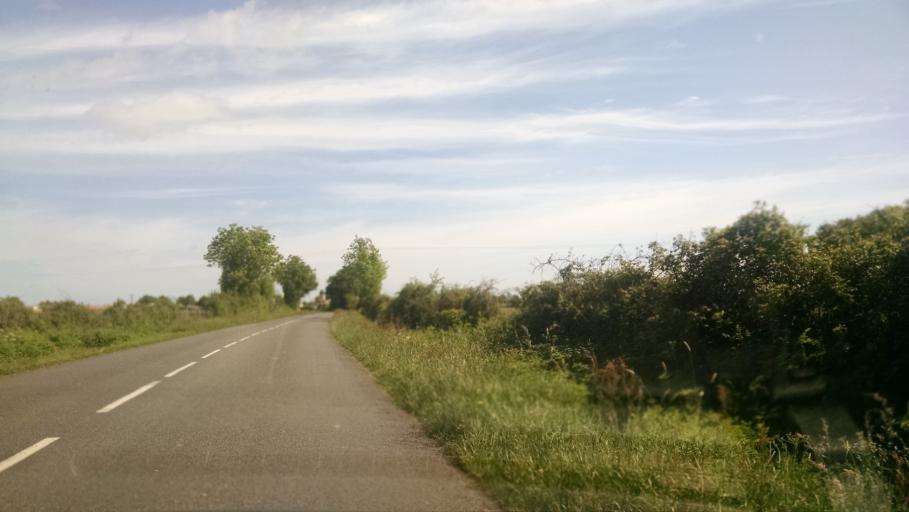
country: FR
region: Pays de la Loire
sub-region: Departement de la Loire-Atlantique
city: Saint-Hilaire-de-Clisson
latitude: 47.0533
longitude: -1.3176
